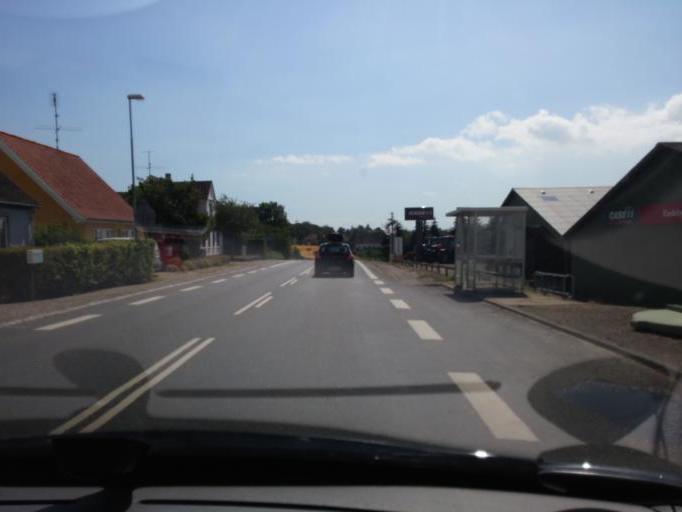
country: DK
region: South Denmark
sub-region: Langeland Kommune
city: Rudkobing
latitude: 54.8398
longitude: 10.7063
